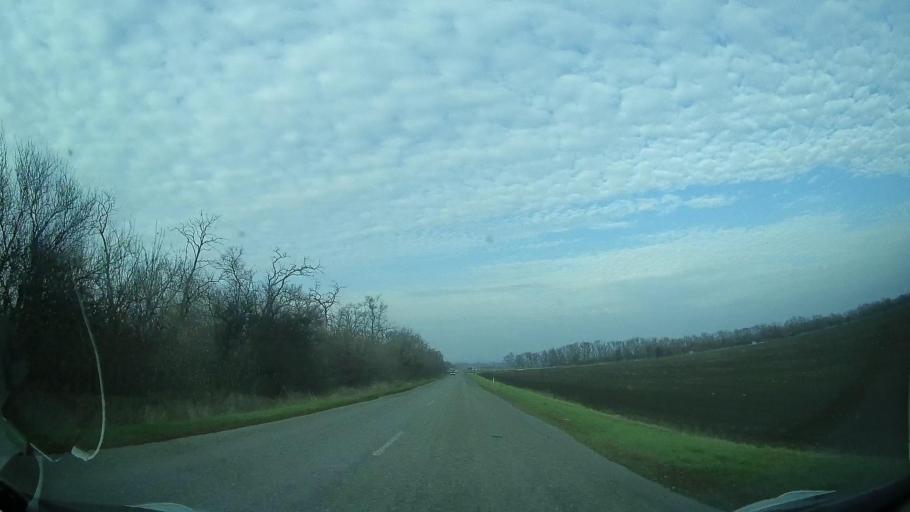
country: RU
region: Rostov
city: Bagayevskaya
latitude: 47.0889
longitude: 40.3915
